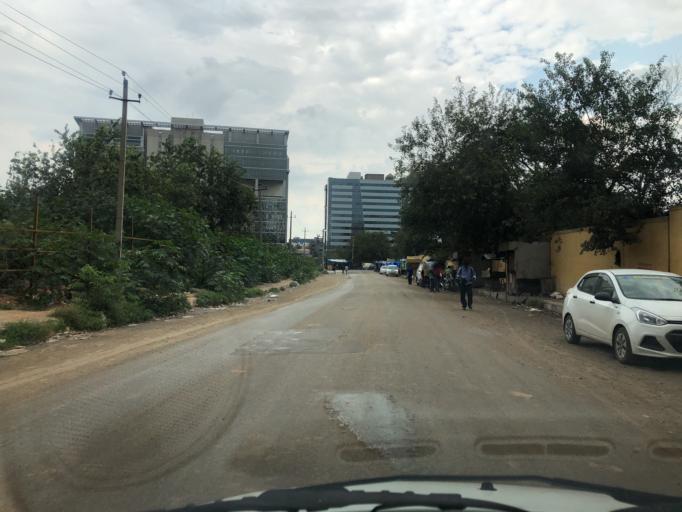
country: IN
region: Karnataka
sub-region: Bangalore Urban
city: Bangalore
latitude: 12.9827
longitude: 77.6957
